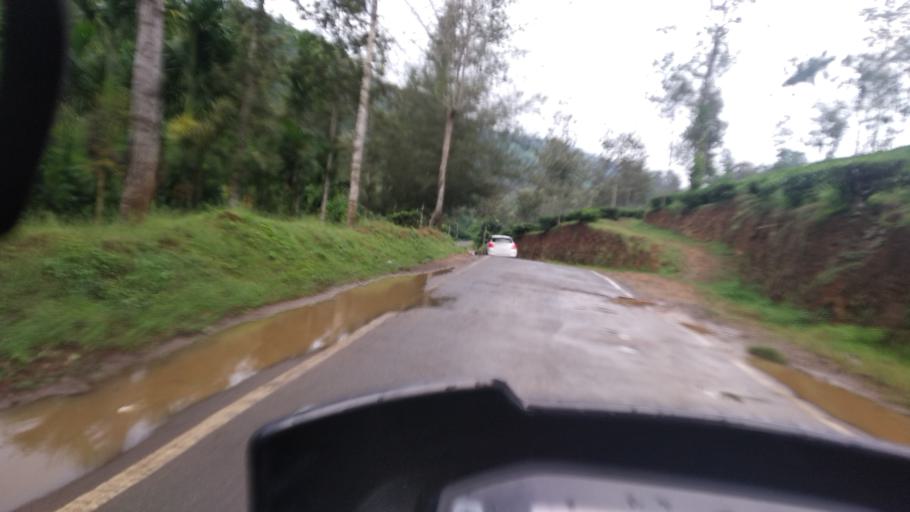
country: IN
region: Tamil Nadu
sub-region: Theni
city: Gudalur
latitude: 9.5668
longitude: 77.0781
